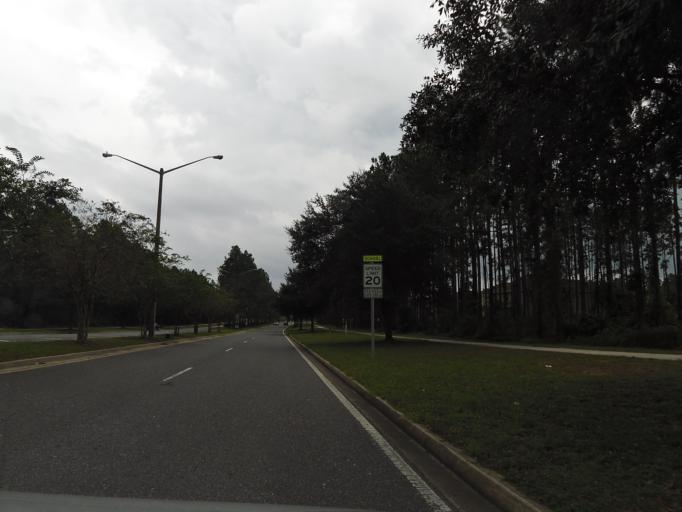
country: US
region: Florida
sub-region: Clay County
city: Lakeside
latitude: 30.1634
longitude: -81.8424
